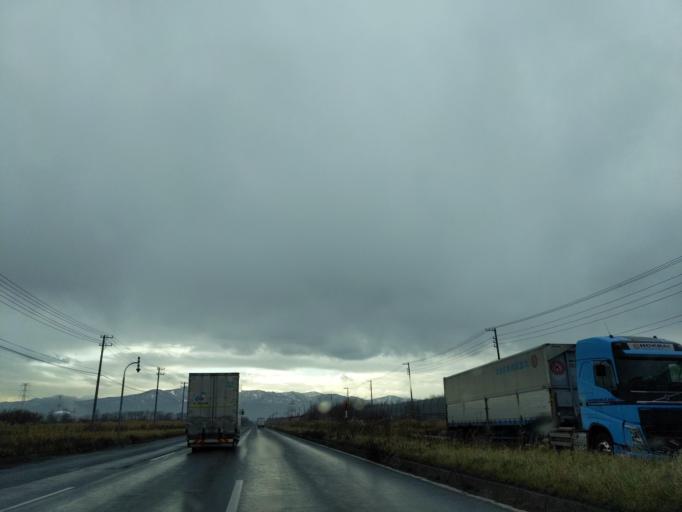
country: JP
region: Hokkaido
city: Ishikari
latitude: 43.1868
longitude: 141.3071
